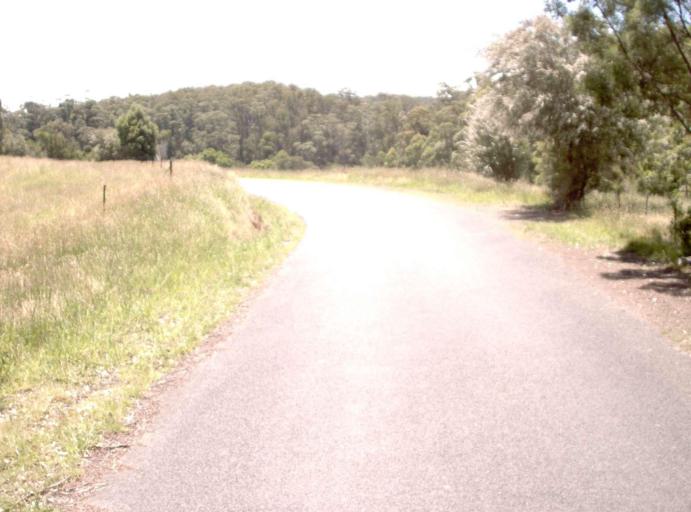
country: AU
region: New South Wales
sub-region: Bombala
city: Bombala
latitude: -37.5223
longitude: 148.9327
